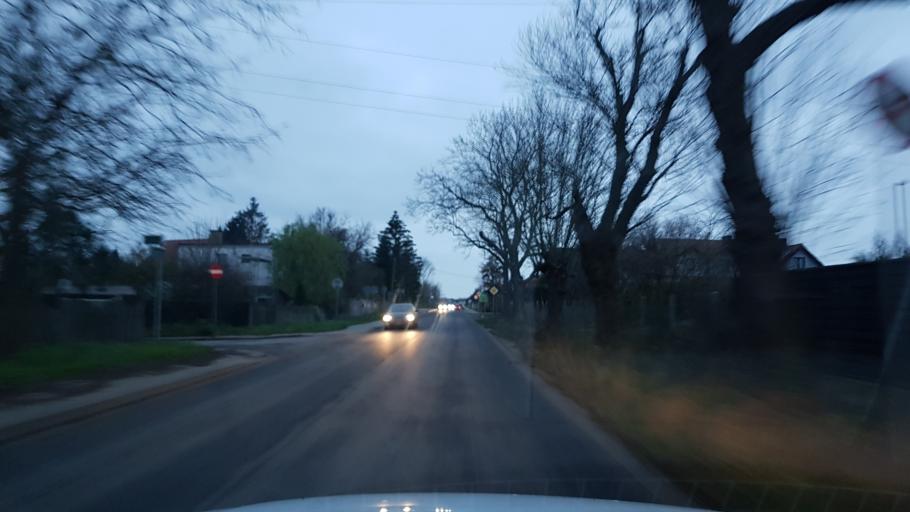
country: PL
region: West Pomeranian Voivodeship
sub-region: Powiat policki
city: Przeclaw
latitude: 53.4190
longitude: 14.4719
